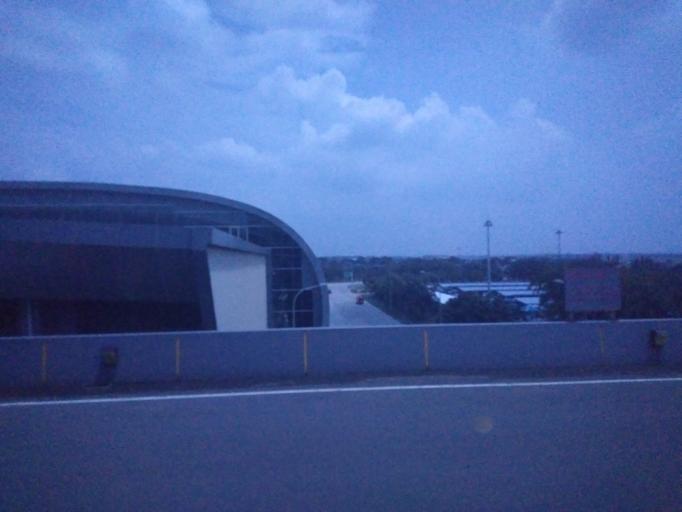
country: ID
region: North Sumatra
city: Percut
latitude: 3.6352
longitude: 98.8784
